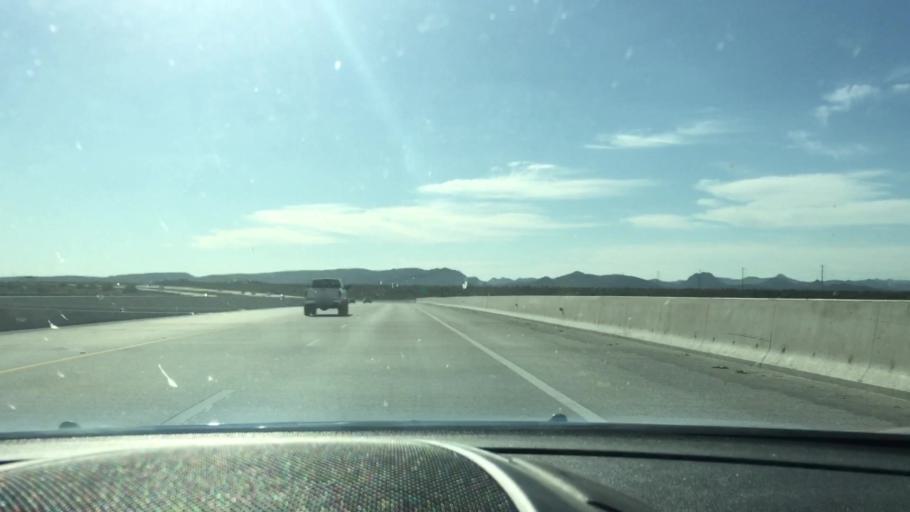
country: US
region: Arizona
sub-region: Maricopa County
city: Anthem
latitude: 33.7841
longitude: -112.2296
